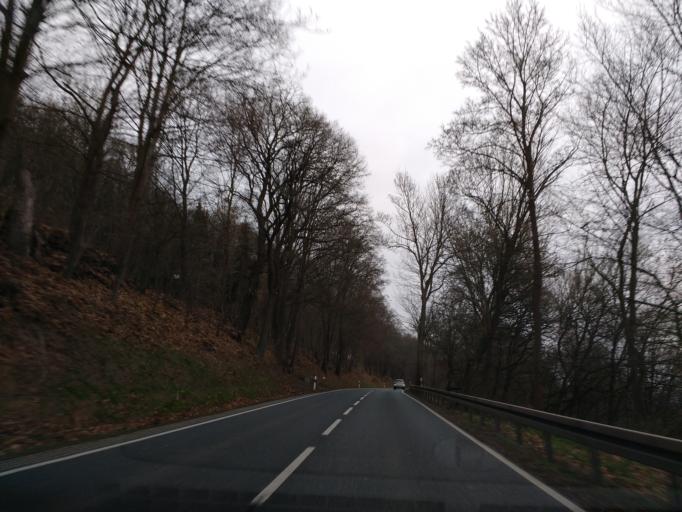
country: DE
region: Hesse
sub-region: Regierungsbezirk Kassel
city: Rotenburg an der Fulda
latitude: 51.0087
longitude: 9.7095
